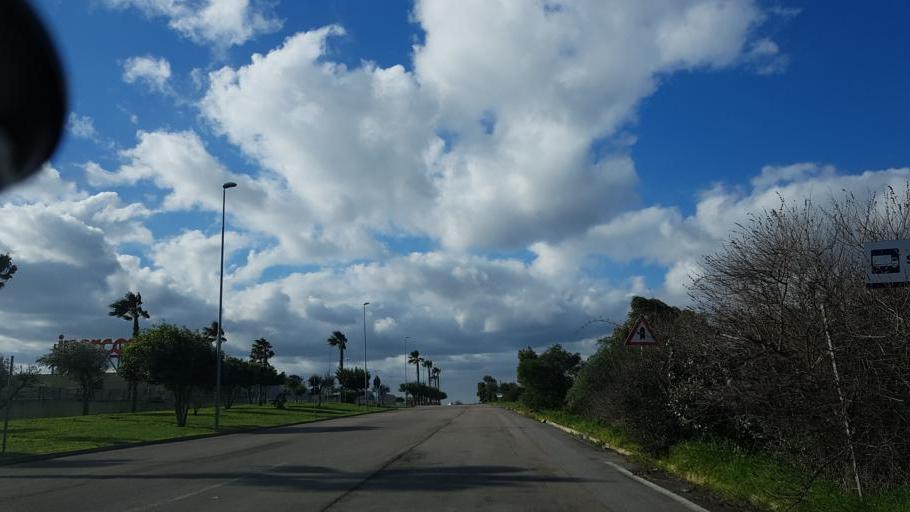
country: IT
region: Apulia
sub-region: Provincia di Brindisi
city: Brindisi
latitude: 40.6210
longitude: 17.9032
